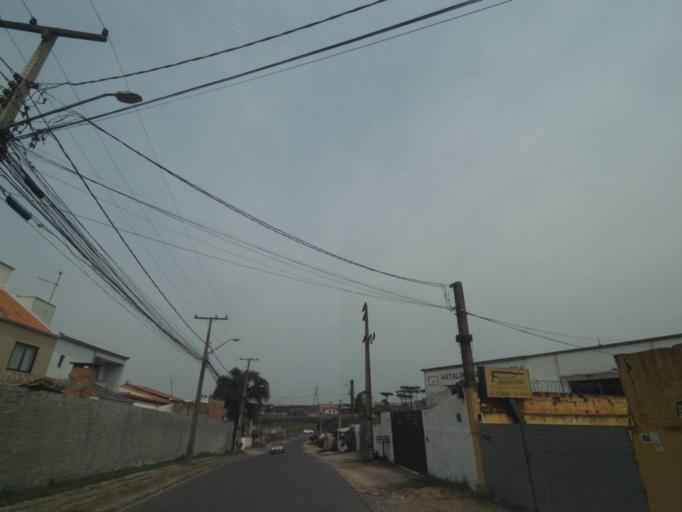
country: BR
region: Parana
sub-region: Sao Jose Dos Pinhais
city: Sao Jose dos Pinhais
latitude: -25.5231
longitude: -49.2917
